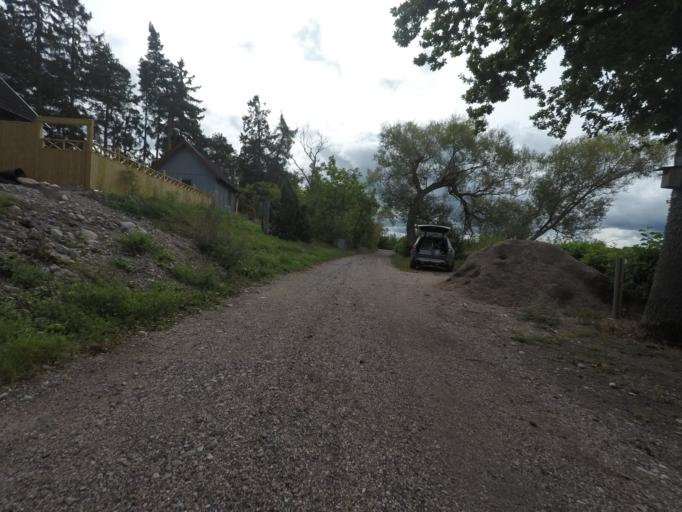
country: SE
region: Vaestmanland
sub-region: Kungsors Kommun
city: Kungsoer
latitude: 59.4675
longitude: 16.0715
